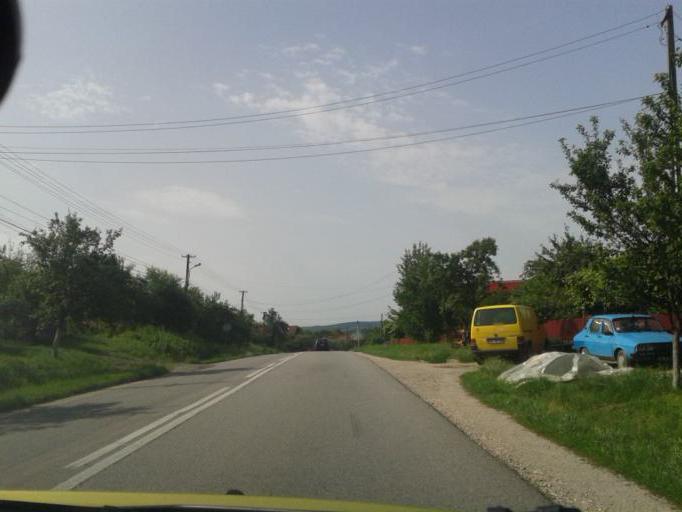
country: RO
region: Valcea
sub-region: Comuna Pietrari
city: Pietrarii de Sus
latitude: 45.1181
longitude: 24.1160
